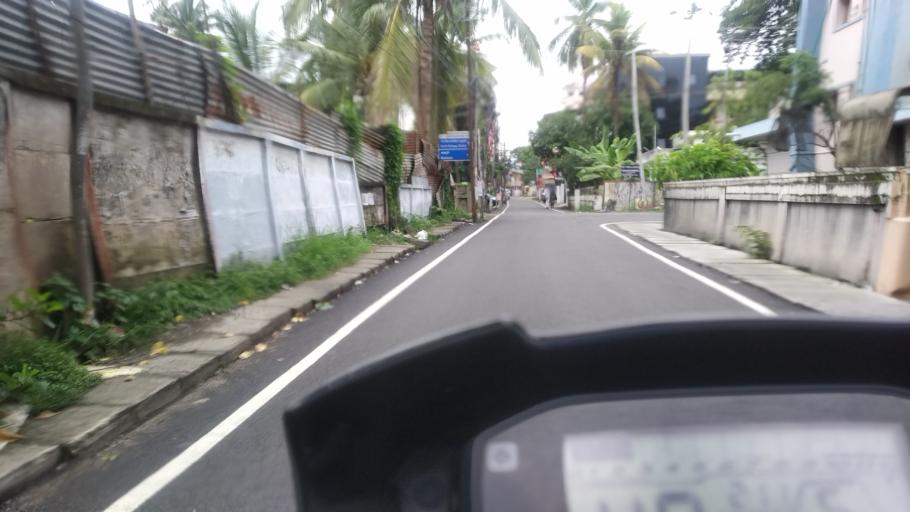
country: IN
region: Kerala
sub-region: Ernakulam
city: Cochin
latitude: 9.9909
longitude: 76.2840
